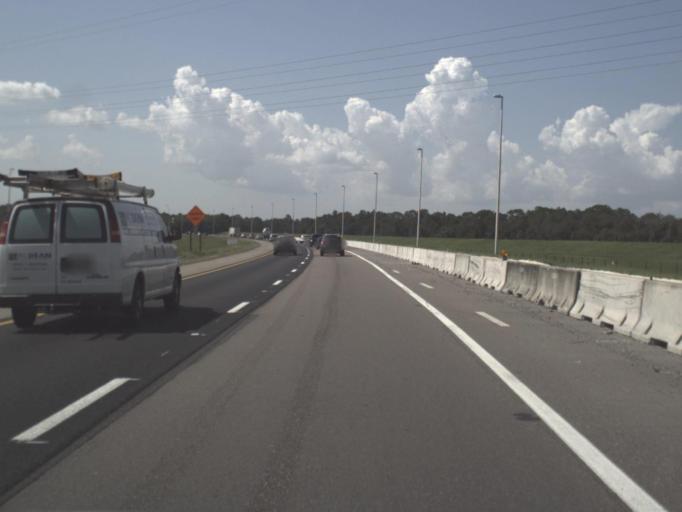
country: US
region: Florida
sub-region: Hillsborough County
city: Pebble Creek
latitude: 28.0918
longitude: -82.3556
